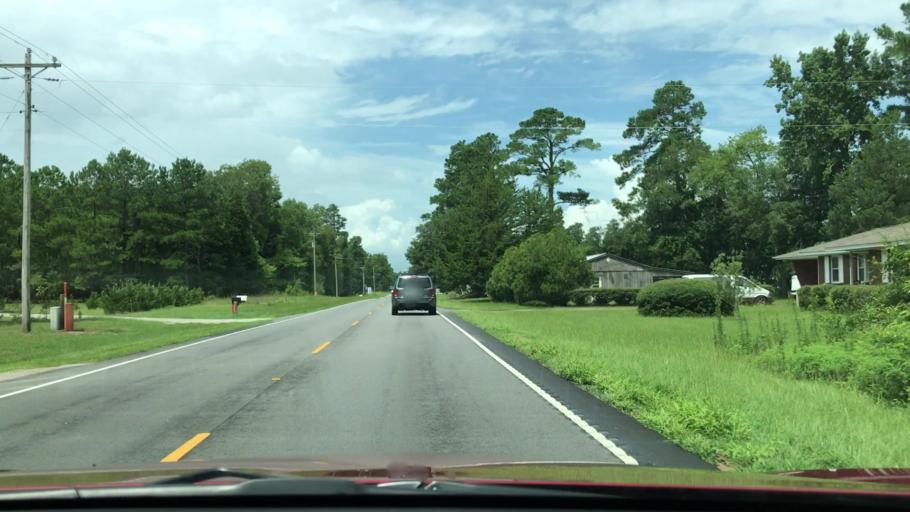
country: US
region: South Carolina
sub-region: Horry County
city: Red Hill
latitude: 33.9026
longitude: -78.8989
